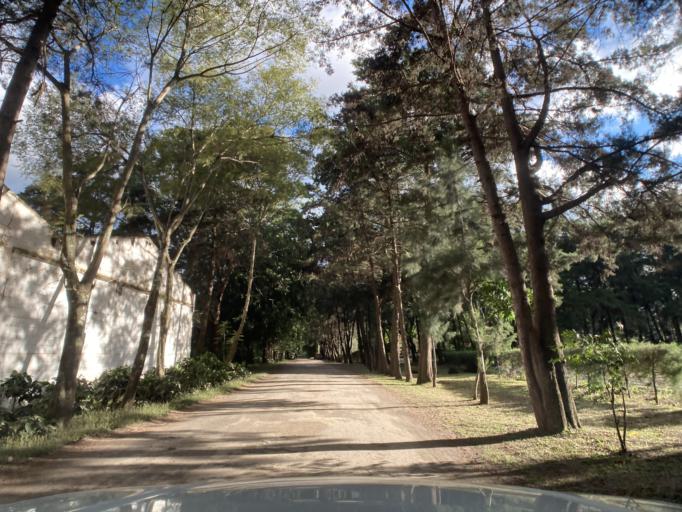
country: GT
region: Sacatepequez
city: Jocotenango
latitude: 14.5736
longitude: -90.7454
